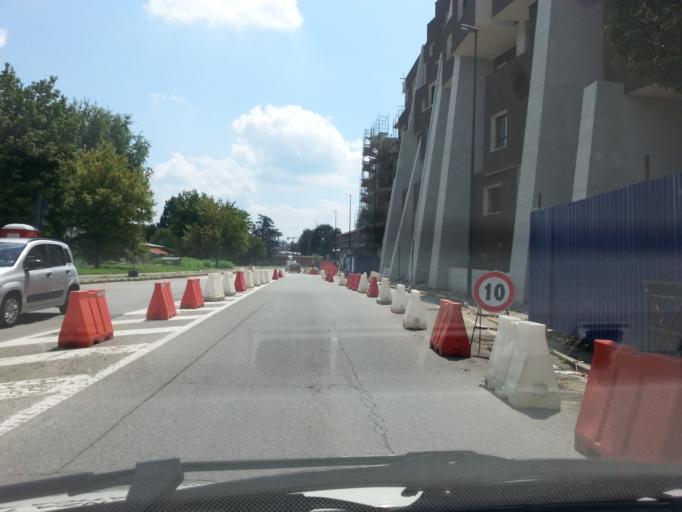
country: IT
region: Piedmont
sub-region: Provincia di Torino
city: Turin
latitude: 45.1023
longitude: 7.6847
